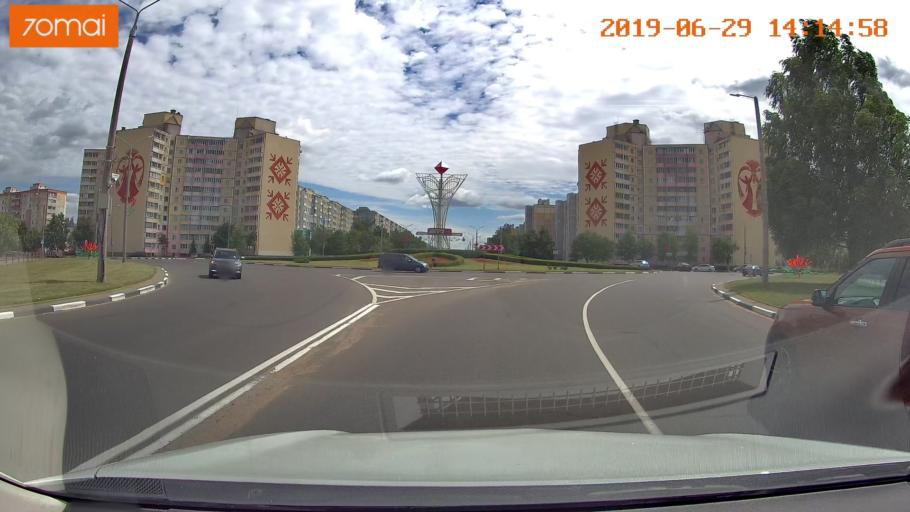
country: BY
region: Minsk
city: Salihorsk
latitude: 52.7922
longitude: 27.5192
